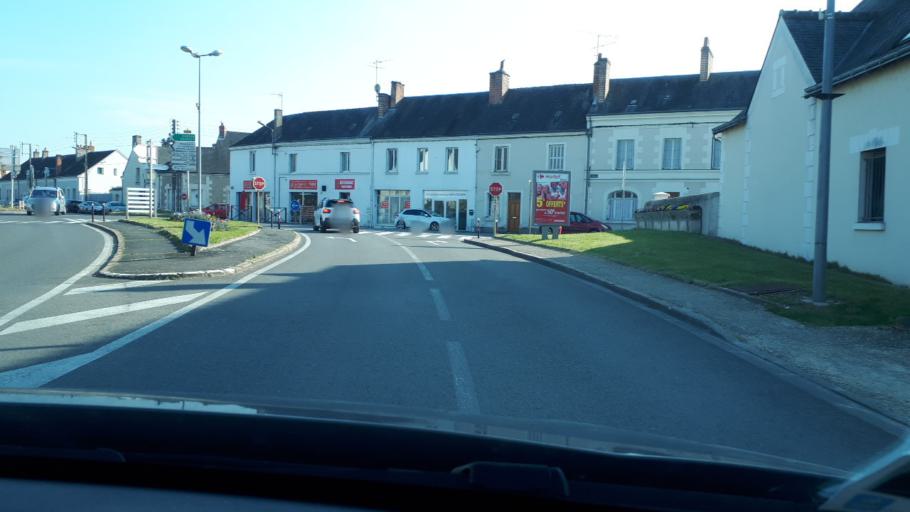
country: FR
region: Centre
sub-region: Departement d'Indre-et-Loire
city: Blere
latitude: 47.3264
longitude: 0.9951
